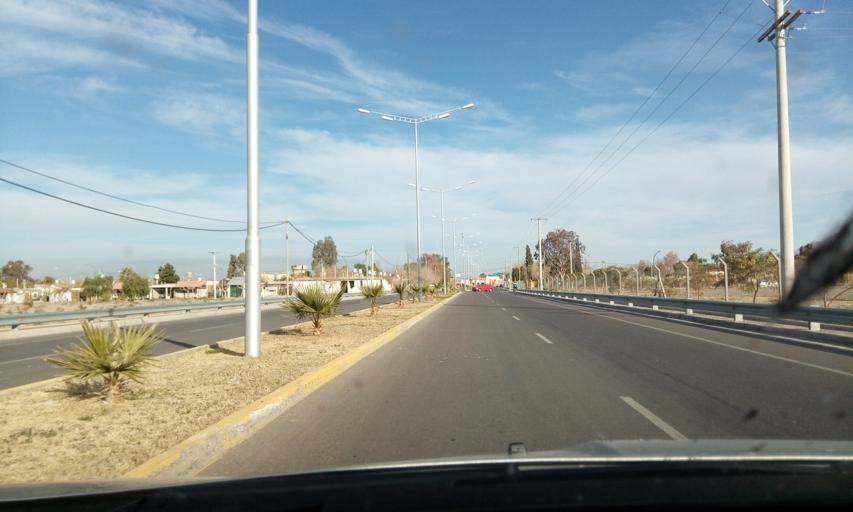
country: AR
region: San Juan
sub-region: Departamento de Rivadavia
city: Rivadavia
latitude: -31.5217
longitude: -68.6285
